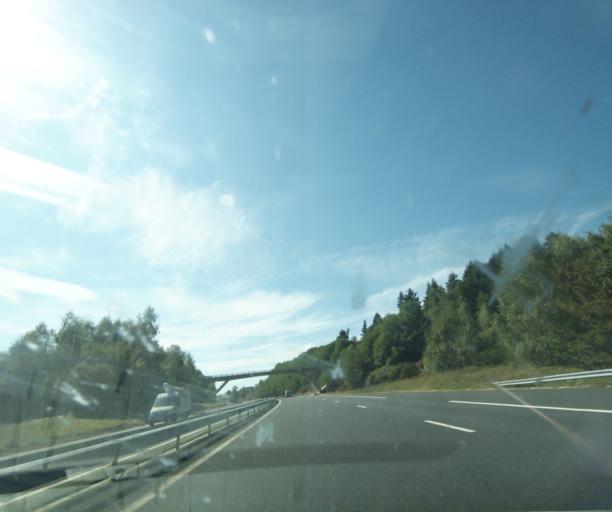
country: FR
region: Limousin
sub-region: Departement de la Correze
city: Naves
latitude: 45.3276
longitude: 1.7583
